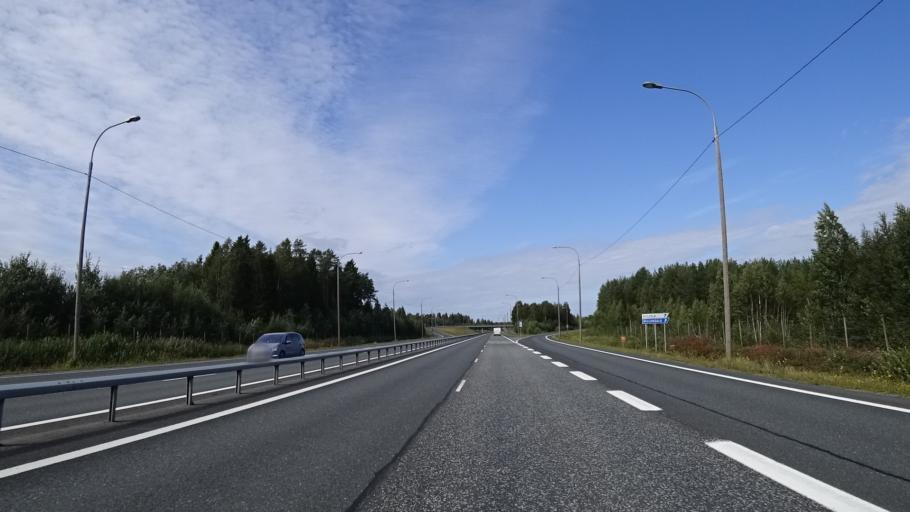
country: FI
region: North Karelia
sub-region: Joensuu
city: Joensuu
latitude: 62.5395
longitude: 29.8513
